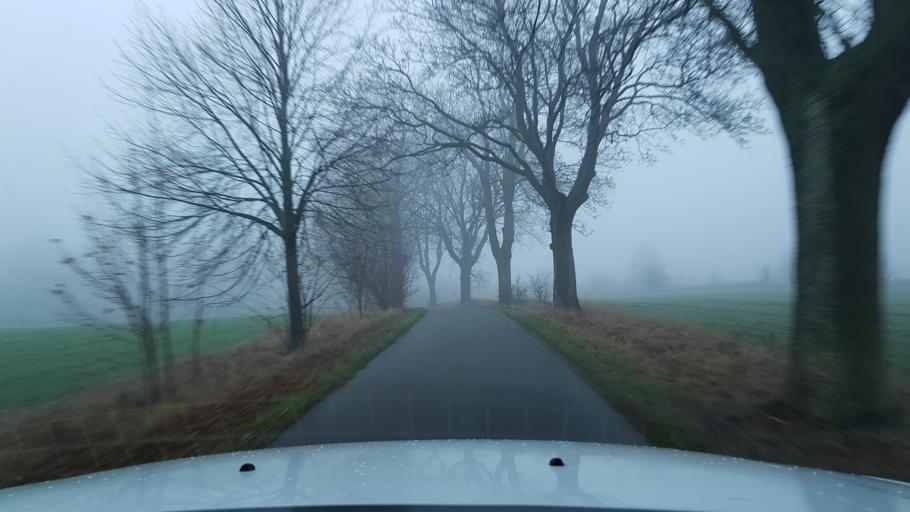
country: DE
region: Brandenburg
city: Mescherin
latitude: 53.2750
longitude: 14.4239
